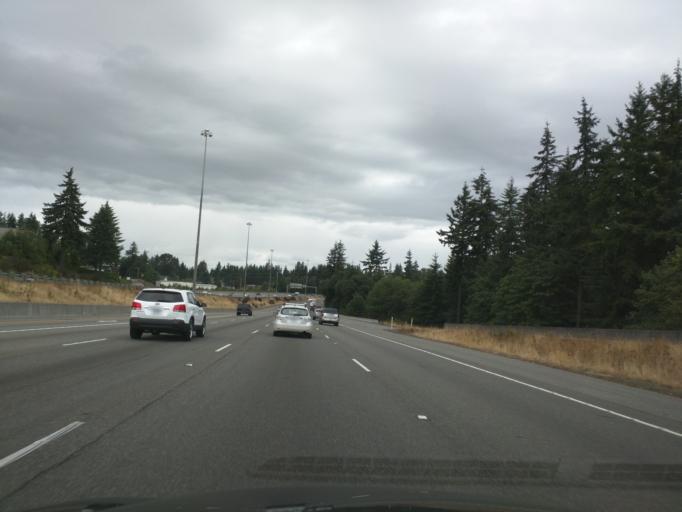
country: US
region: Washington
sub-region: Snohomish County
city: Everett
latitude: 47.9225
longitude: -122.2048
